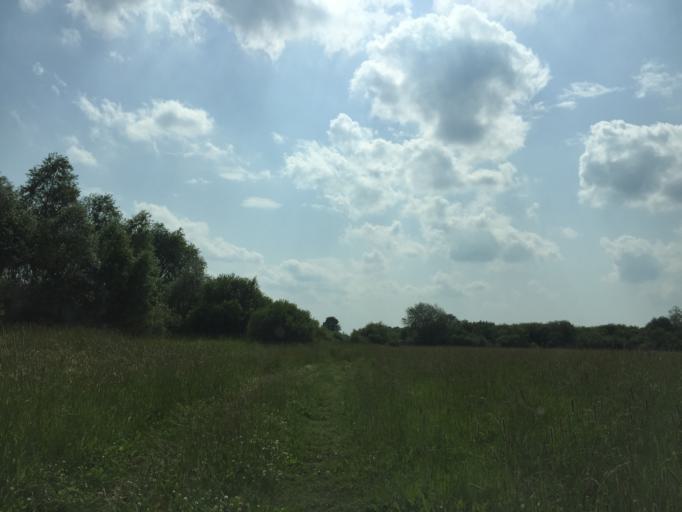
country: LV
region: Jelgava
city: Jelgava
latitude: 56.6829
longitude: 23.7189
